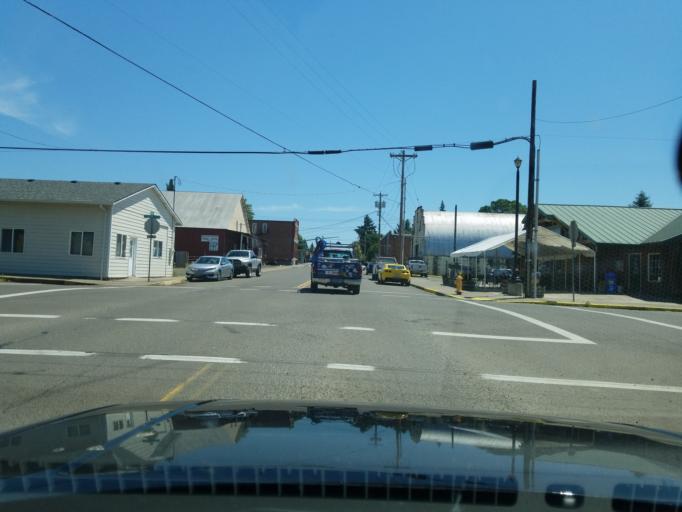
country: US
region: Oregon
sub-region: Yamhill County
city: Yamhill
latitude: 45.3415
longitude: -123.1895
